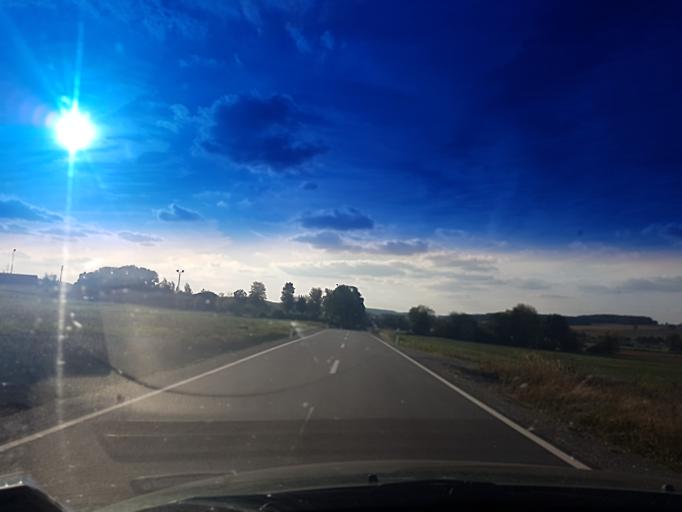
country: DE
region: Bavaria
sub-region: Regierungsbezirk Mittelfranken
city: Wachenroth
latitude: 49.7391
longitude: 10.6763
